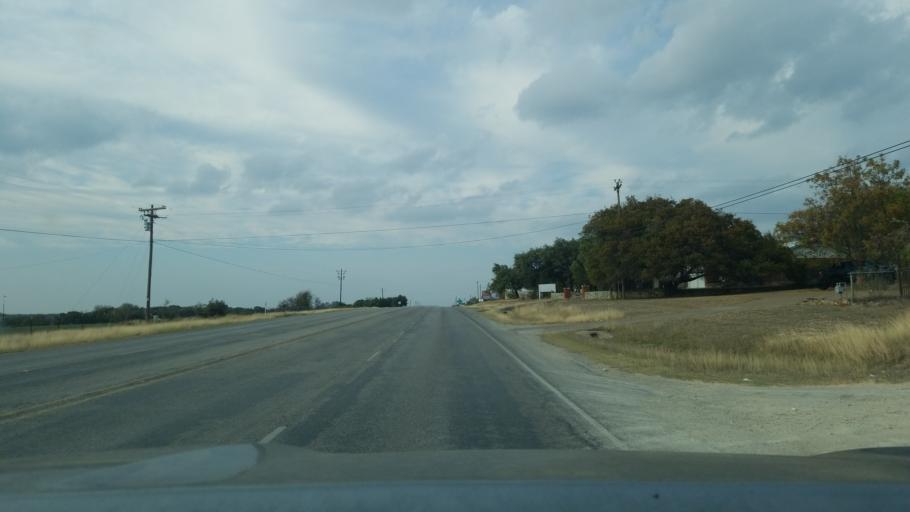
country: US
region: Texas
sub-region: Mills County
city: Goldthwaite
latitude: 31.4807
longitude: -98.5703
